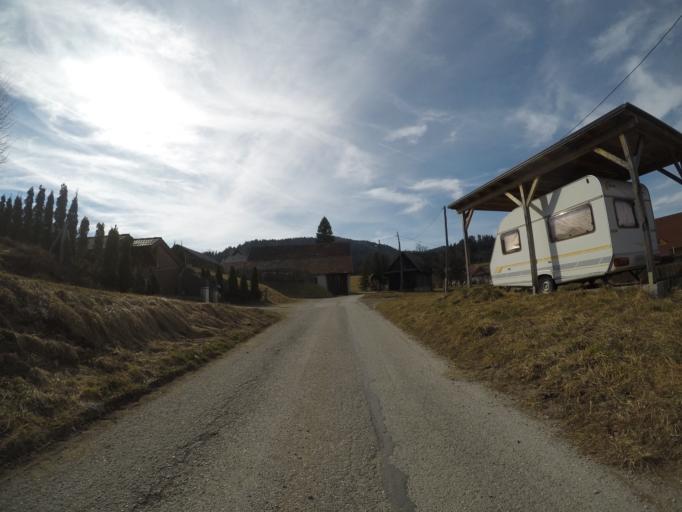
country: SI
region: Lovrenc na Pohorju
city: Lovrenc na Pohorju
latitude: 46.5333
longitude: 15.3819
